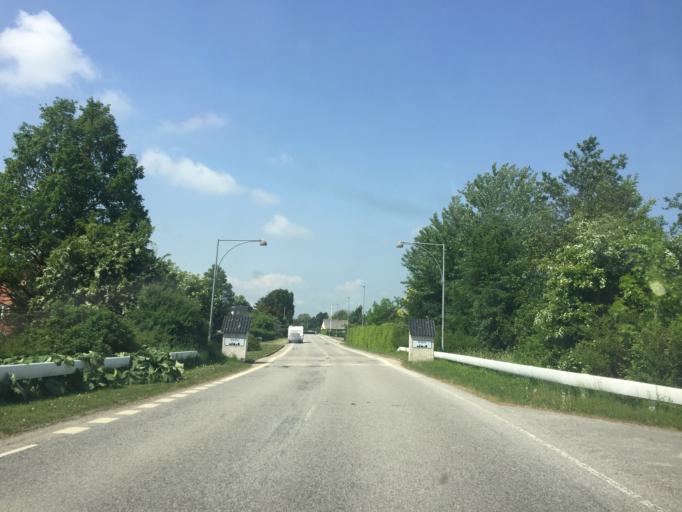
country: DK
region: South Denmark
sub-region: Kolding Kommune
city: Sonder Bjert
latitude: 55.3791
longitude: 9.5825
